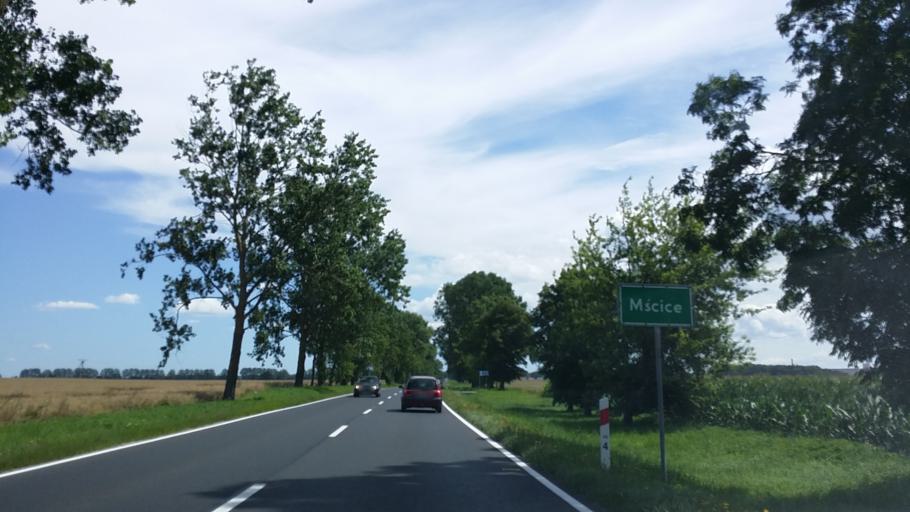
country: PL
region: West Pomeranian Voivodeship
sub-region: Powiat koszalinski
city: Mielno
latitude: 54.2235
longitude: 16.0497
